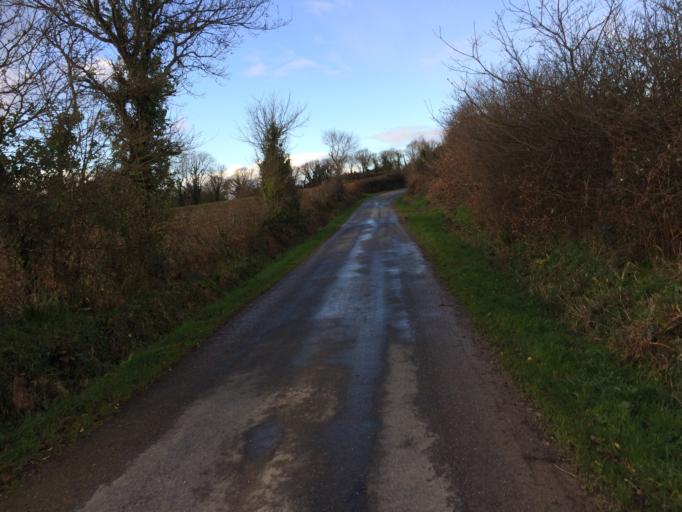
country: FR
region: Brittany
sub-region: Departement du Finistere
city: Hopital-Camfrout
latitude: 48.3318
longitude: -4.2690
